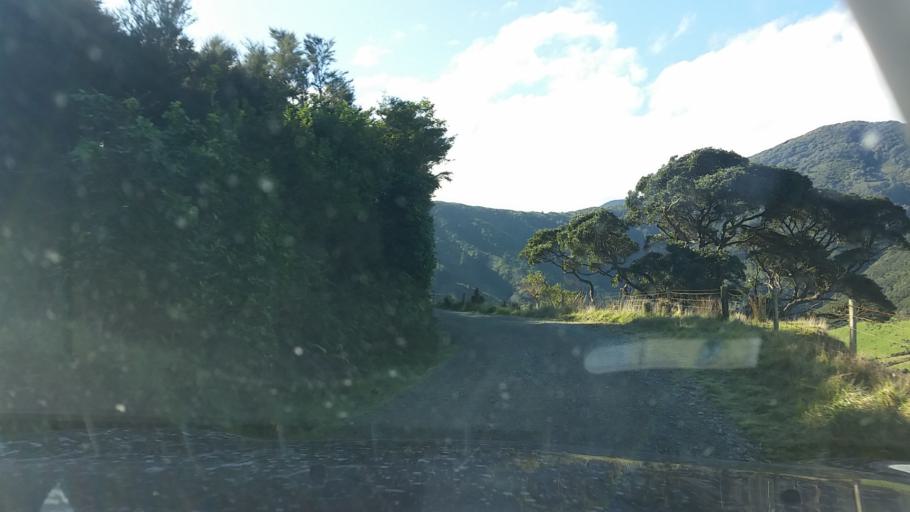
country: NZ
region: Marlborough
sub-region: Marlborough District
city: Picton
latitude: -41.1461
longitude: 174.0505
